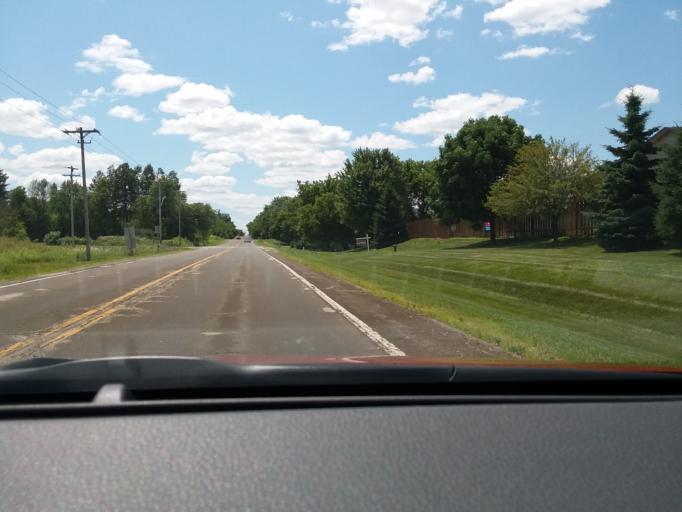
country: US
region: Wisconsin
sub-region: Dane County
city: Windsor
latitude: 43.2245
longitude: -89.3436
